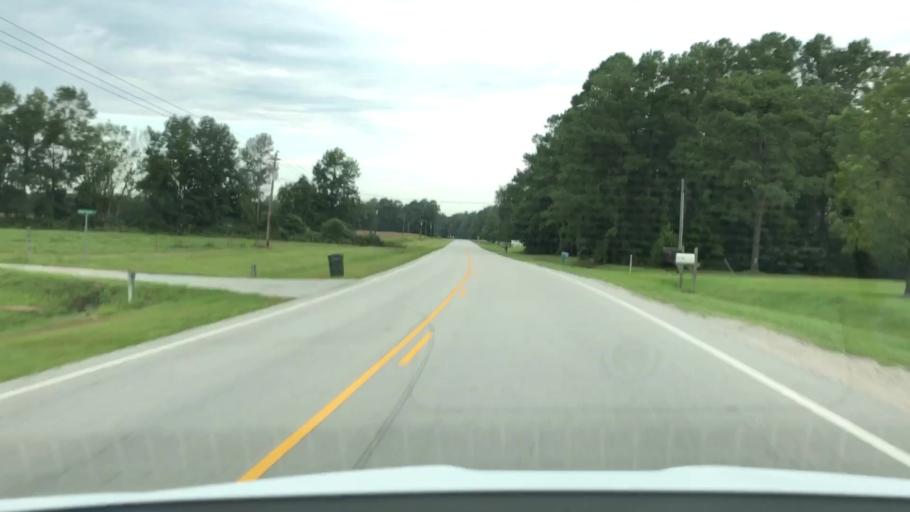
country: US
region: North Carolina
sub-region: Jones County
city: Trenton
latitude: 35.0288
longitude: -77.3107
